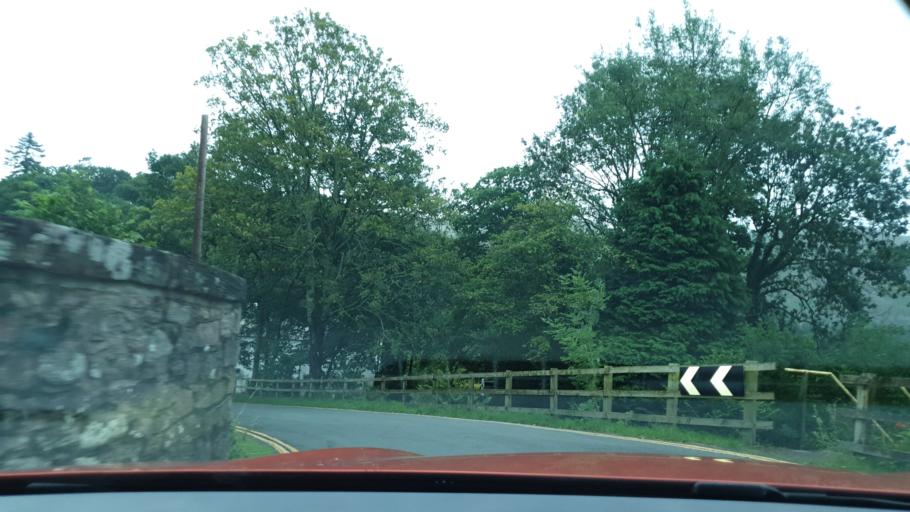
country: GB
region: England
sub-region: Cumbria
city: Seascale
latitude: 54.3872
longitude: -3.3172
